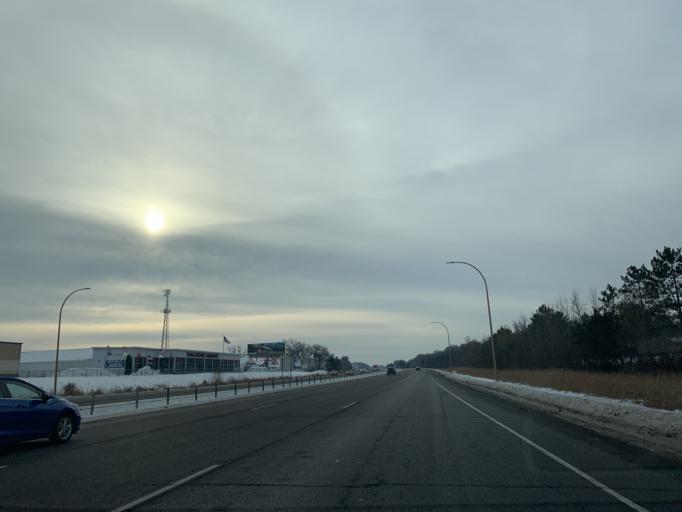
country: US
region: Minnesota
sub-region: Chisago County
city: Wyoming
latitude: 45.3339
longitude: -93.0050
